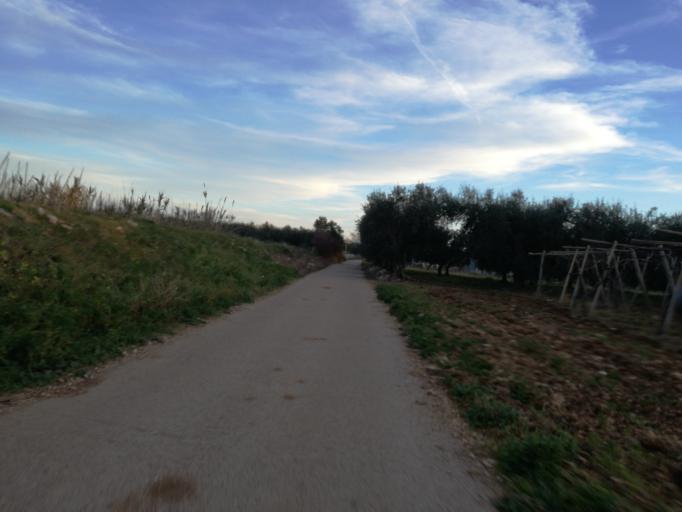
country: IT
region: Apulia
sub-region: Provincia di Bari
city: Lamie
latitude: 41.0217
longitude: 16.8718
